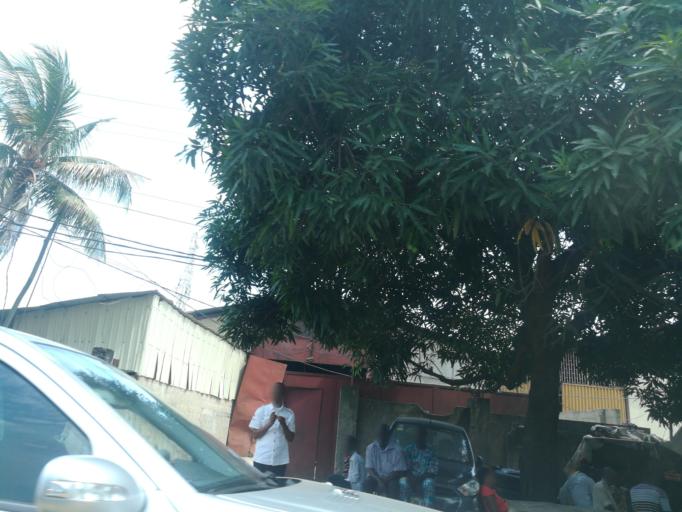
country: NG
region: Lagos
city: Ikeja
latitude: 6.6096
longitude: 3.3661
